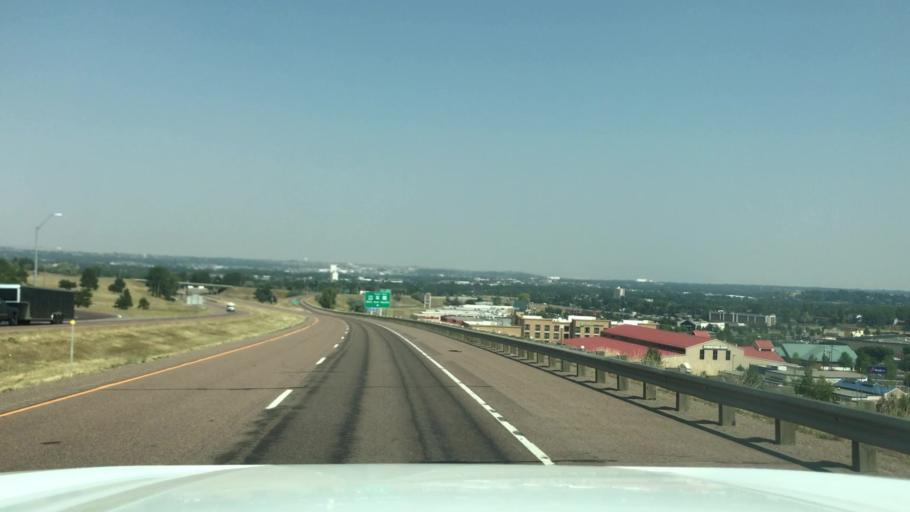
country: US
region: Montana
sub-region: Cascade County
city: Great Falls
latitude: 47.4798
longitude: -111.3496
